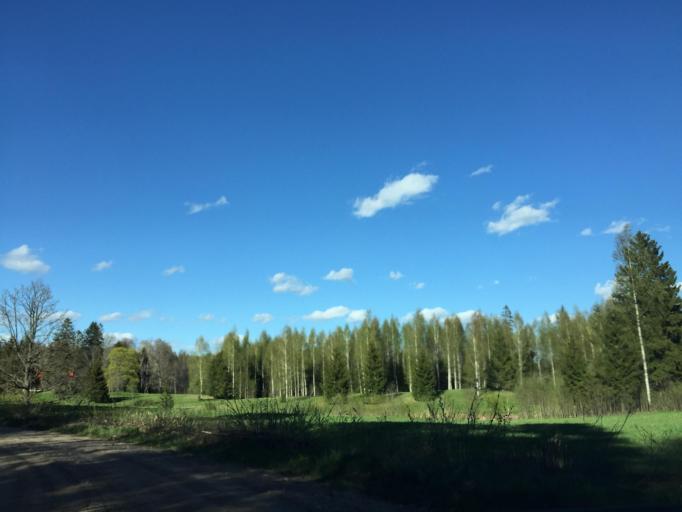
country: LV
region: Madonas Rajons
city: Madona
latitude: 56.8652
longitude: 25.9707
